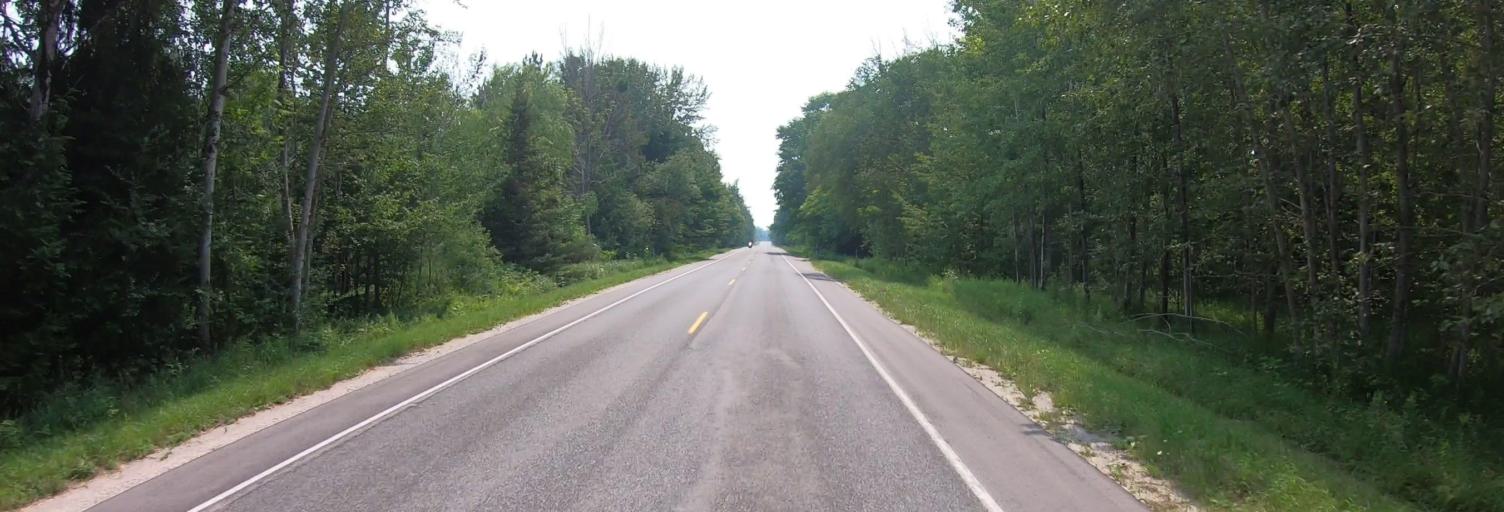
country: US
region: Michigan
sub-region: Leelanau County
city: Leland
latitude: 45.2016
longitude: -85.5455
